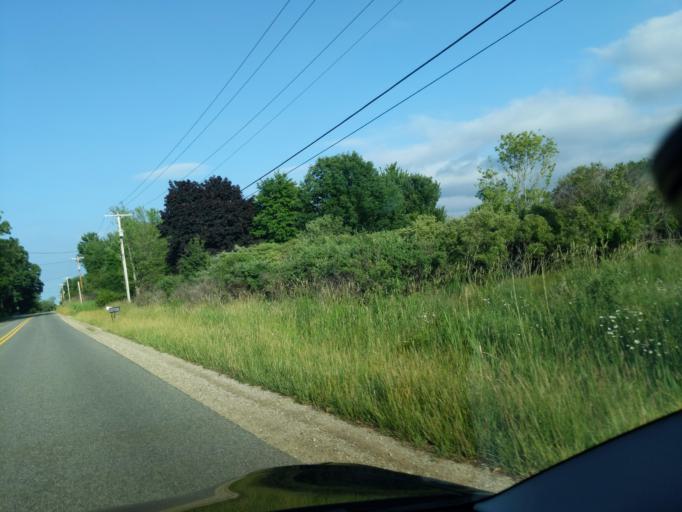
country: US
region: Michigan
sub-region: Muskegon County
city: Whitehall
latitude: 43.4031
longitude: -86.3249
